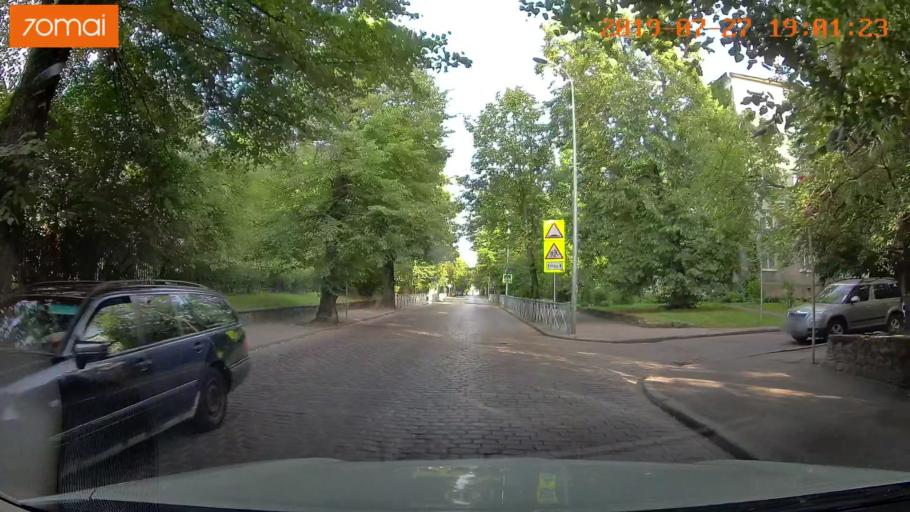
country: RU
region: Kaliningrad
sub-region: Gorod Kaliningrad
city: Kaliningrad
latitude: 54.7265
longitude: 20.4880
